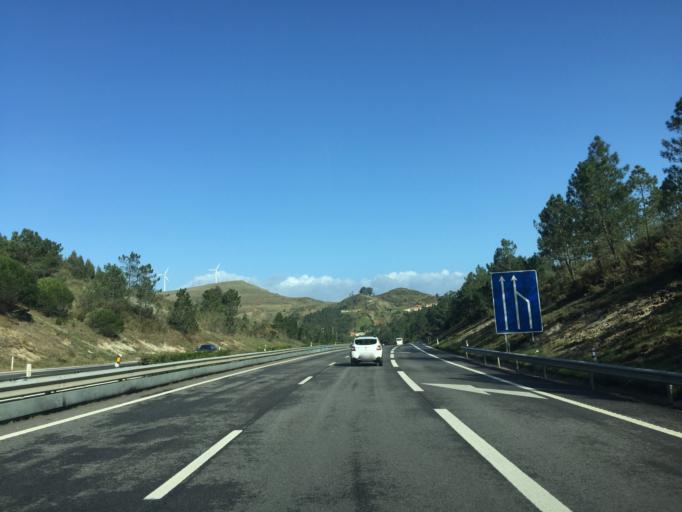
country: PT
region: Lisbon
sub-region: Sobral de Monte Agraco
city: Sobral de Monte Agraco
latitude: 39.0202
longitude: -9.2174
